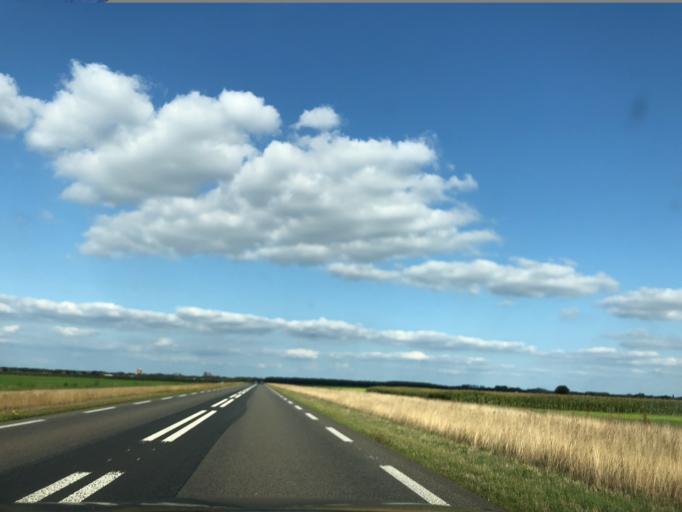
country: NL
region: Groningen
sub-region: Gemeente Stadskanaal
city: Stadskanaal
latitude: 52.9694
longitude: 6.9154
